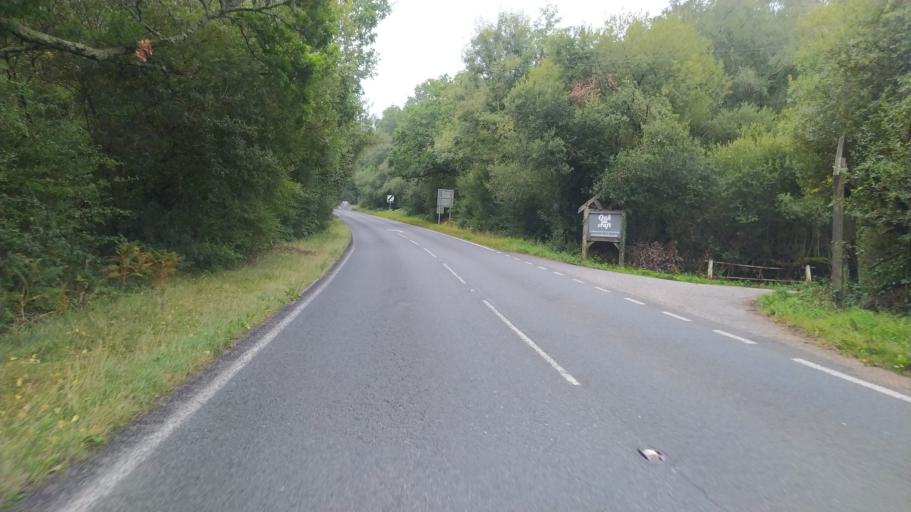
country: GB
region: England
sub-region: Hampshire
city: New Milton
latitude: 50.8026
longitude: -1.6731
